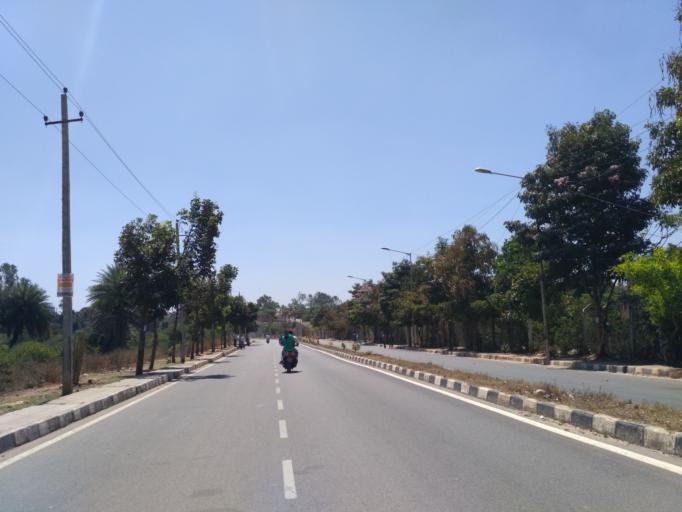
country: IN
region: Karnataka
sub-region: Bangalore Urban
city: Yelahanka
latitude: 13.0919
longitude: 77.5909
